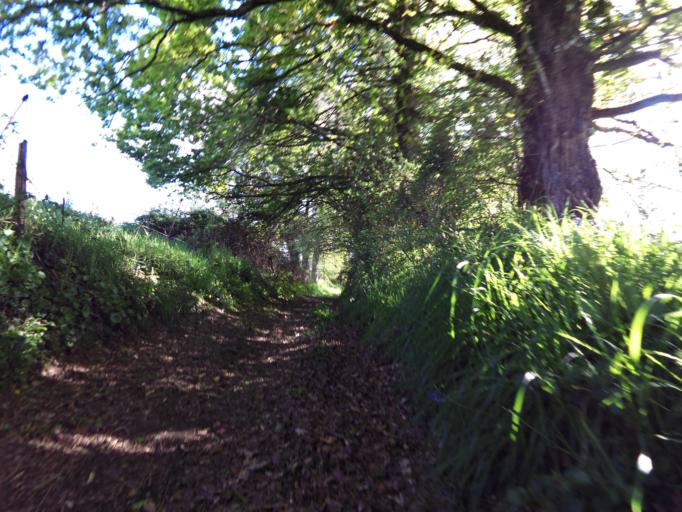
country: FR
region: Brittany
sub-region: Departement d'Ille-et-Vilaine
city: Pance
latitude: 47.9002
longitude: -1.6091
